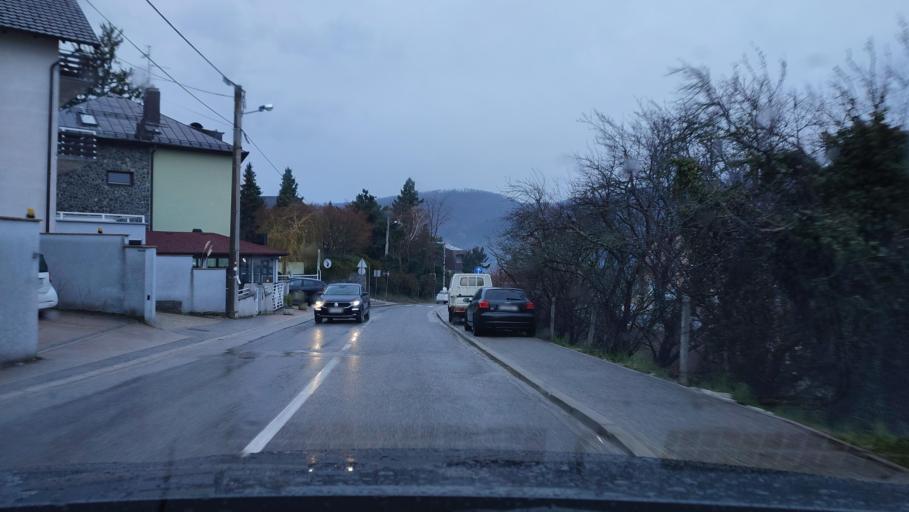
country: HR
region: Grad Zagreb
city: Zagreb
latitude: 45.8505
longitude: 15.9525
